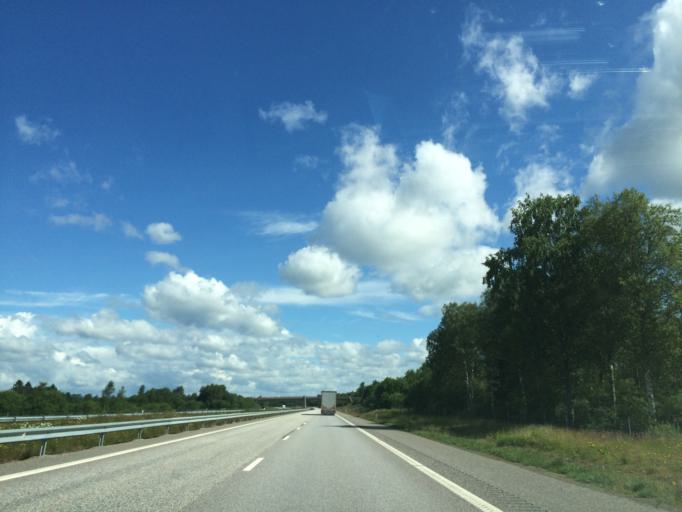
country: SE
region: Kronoberg
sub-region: Markaryds Kommun
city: Stromsnasbruk
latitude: 56.6398
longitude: 13.7999
